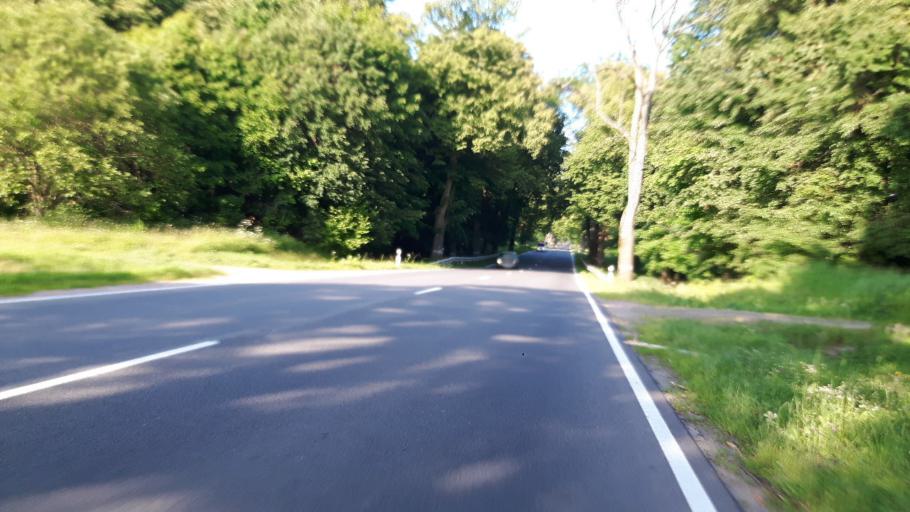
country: RU
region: Kaliningrad
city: Ladushkin
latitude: 54.4977
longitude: 20.0795
